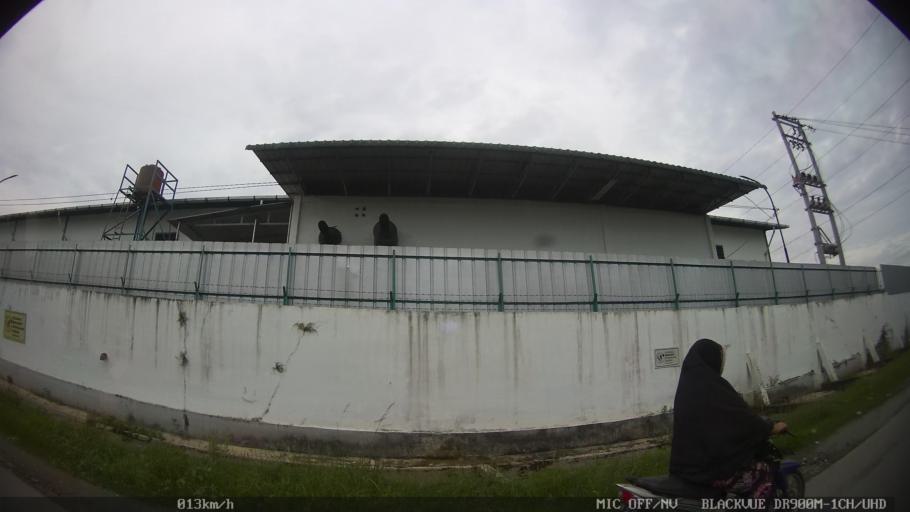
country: ID
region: North Sumatra
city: Sunggal
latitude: 3.6144
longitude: 98.5895
